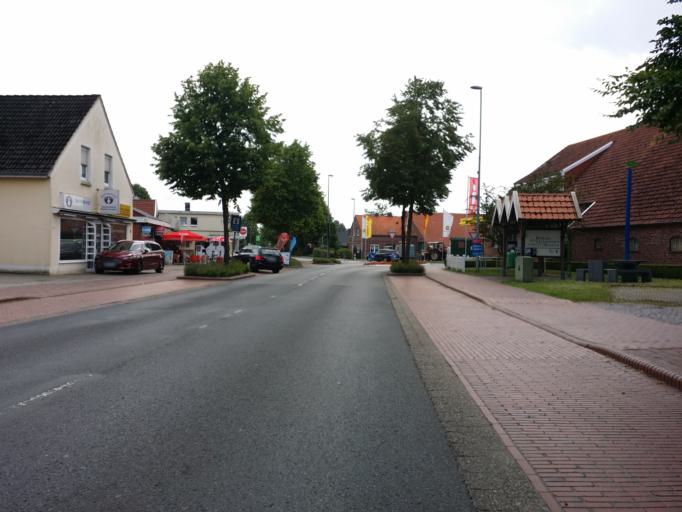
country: DE
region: Lower Saxony
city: Friedeburg
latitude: 53.4520
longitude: 7.8399
